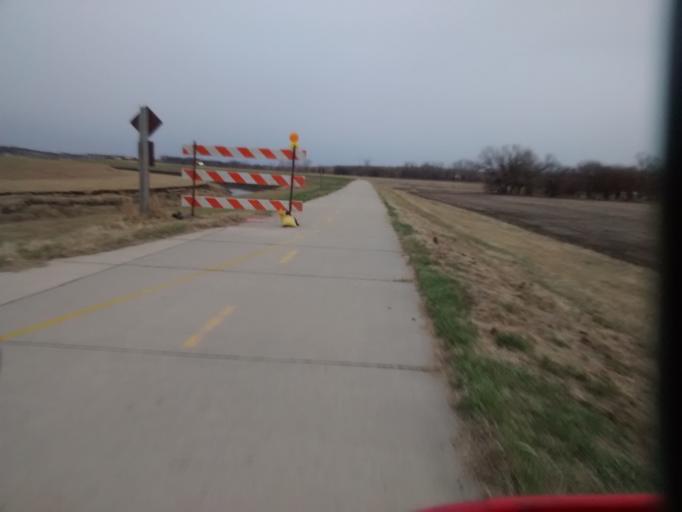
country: US
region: Nebraska
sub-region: Sarpy County
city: Offutt Air Force Base
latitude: 41.1425
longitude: -95.9487
